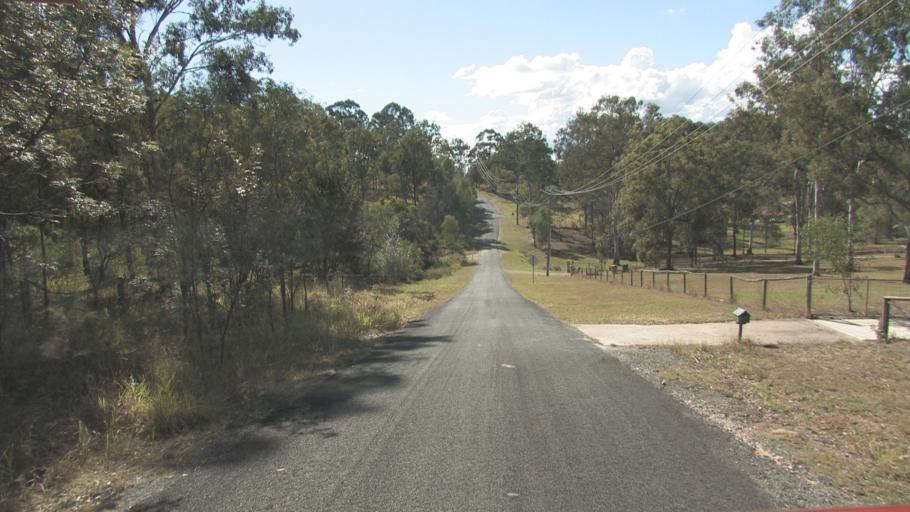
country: AU
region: Queensland
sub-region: Logan
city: Chambers Flat
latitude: -27.8130
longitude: 153.0891
